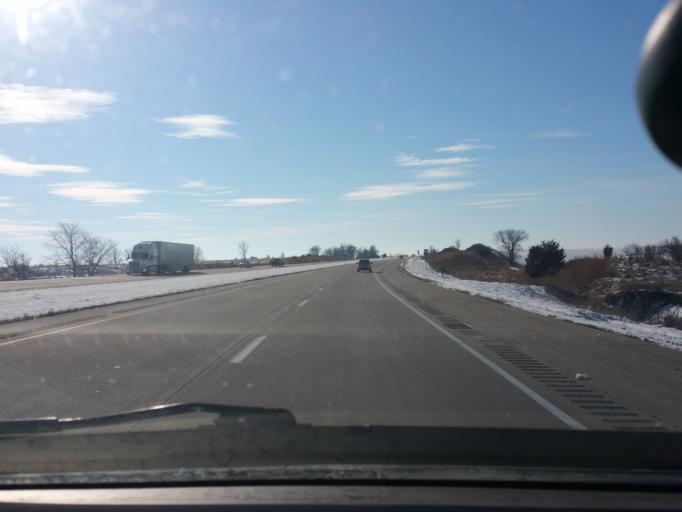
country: US
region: Iowa
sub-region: Clarke County
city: Osceola
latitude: 40.9662
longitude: -93.7975
